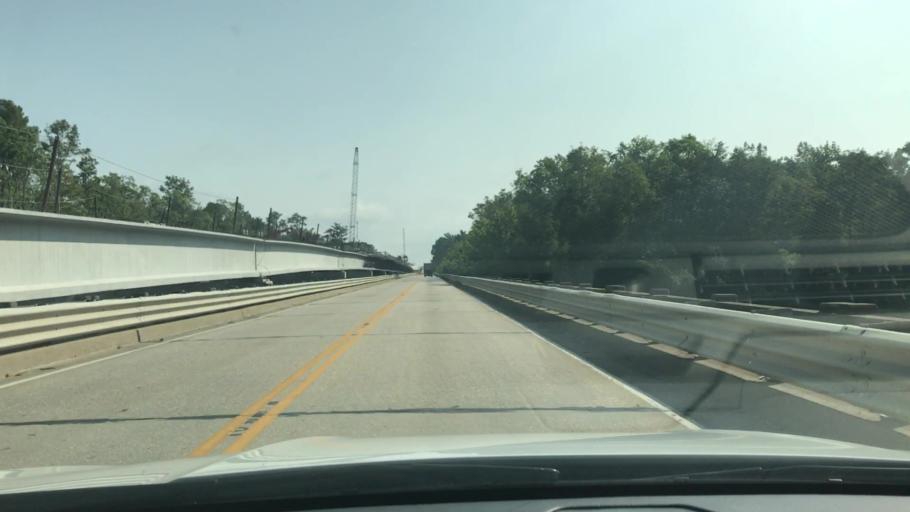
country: US
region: South Carolina
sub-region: Georgetown County
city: Murrells Inlet
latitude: 33.6544
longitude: -79.1630
